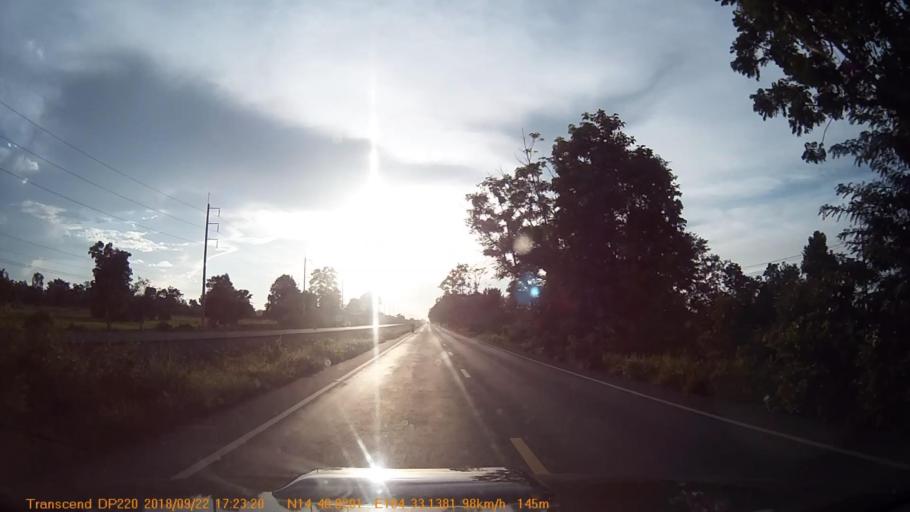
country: TH
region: Sisaket
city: Kantharalak
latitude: 14.6804
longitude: 104.5519
